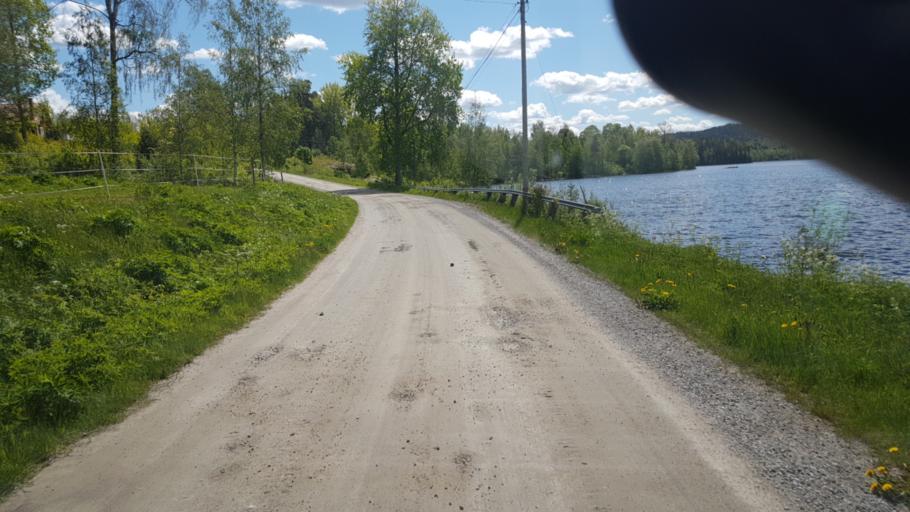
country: SE
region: Vaermland
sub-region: Arvika Kommun
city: Arvika
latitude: 59.7212
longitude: 12.8375
